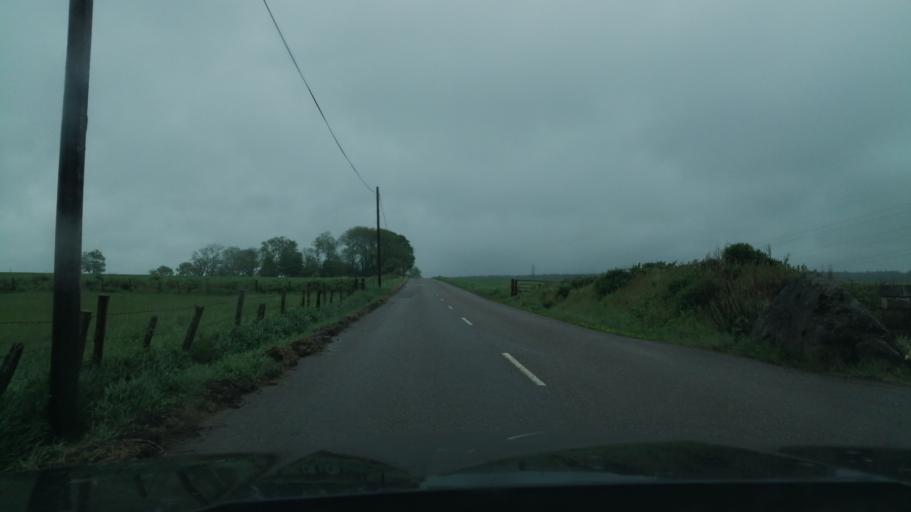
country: GB
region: Scotland
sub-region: Aberdeenshire
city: Huntly
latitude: 57.5475
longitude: -2.8187
